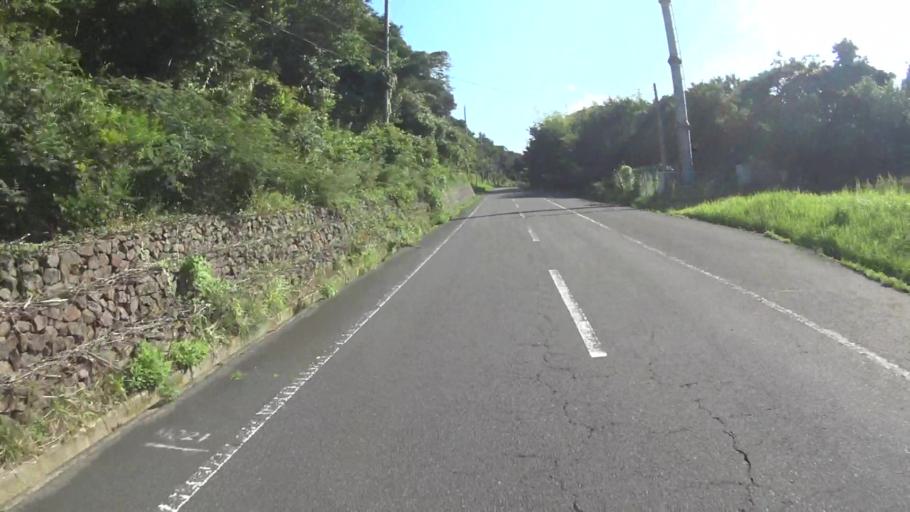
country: JP
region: Kyoto
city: Miyazu
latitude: 35.7063
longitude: 135.0692
